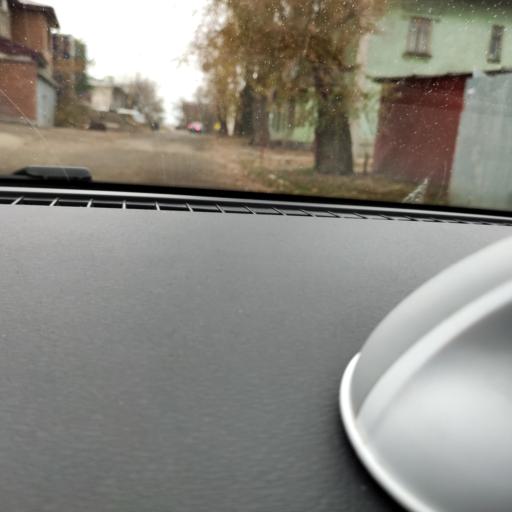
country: RU
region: Samara
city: Samara
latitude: 53.1818
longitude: 50.1897
